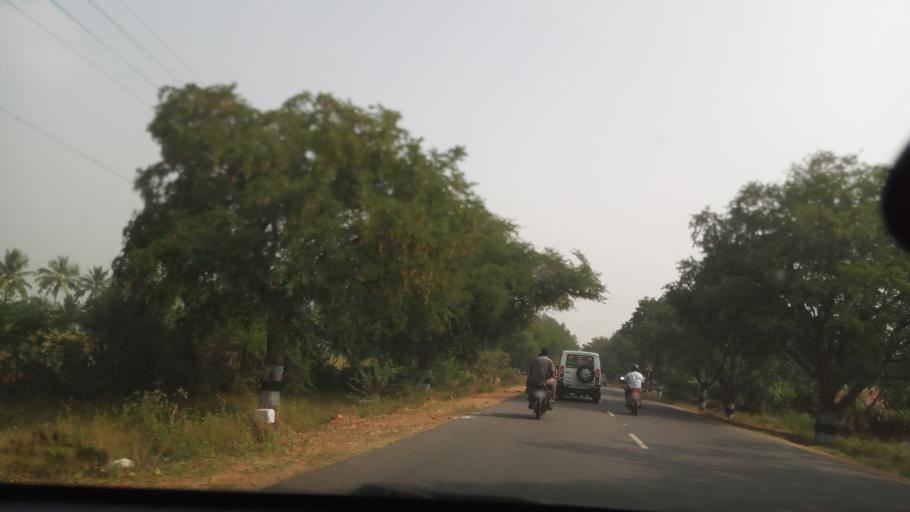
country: IN
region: Tamil Nadu
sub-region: Erode
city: Sathyamangalam
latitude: 11.4395
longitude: 77.2057
